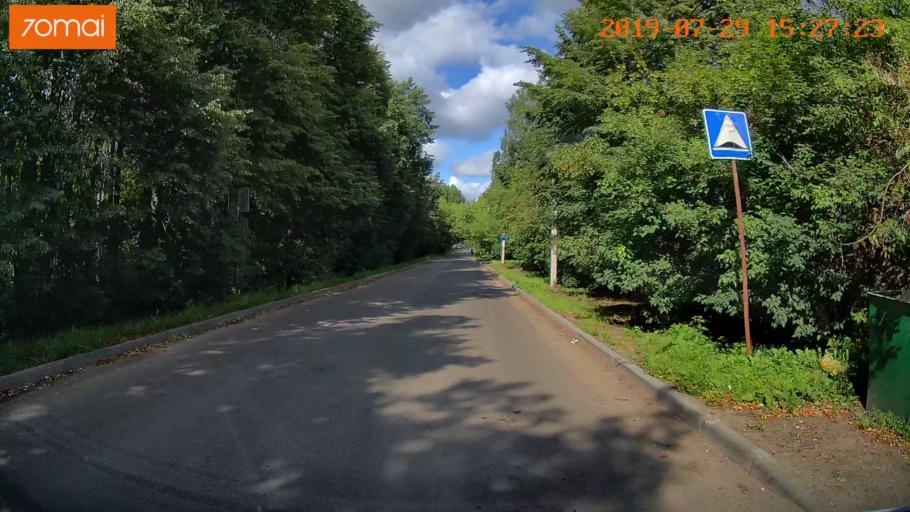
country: RU
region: Ivanovo
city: Bogorodskoye
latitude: 57.0222
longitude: 41.0078
